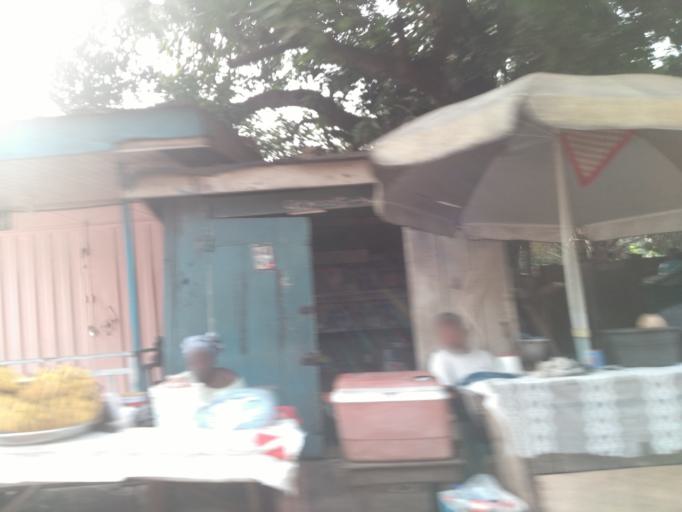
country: GH
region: Ashanti
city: Kumasi
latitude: 6.6905
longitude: -1.6100
